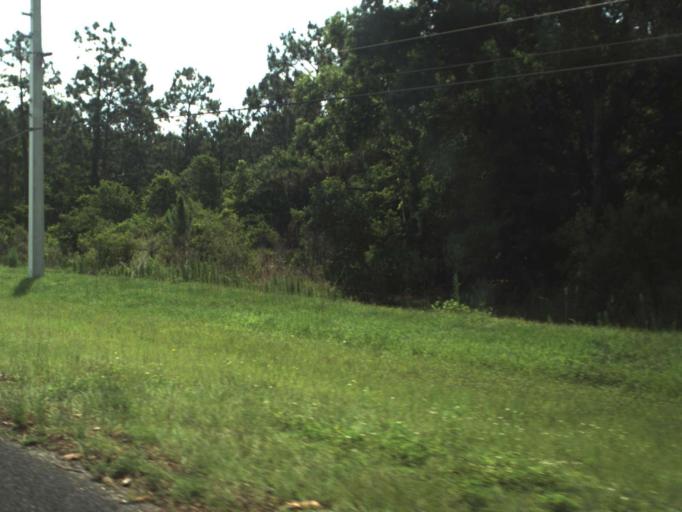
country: US
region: Florida
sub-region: Volusia County
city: Lake Helen
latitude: 29.0293
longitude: -81.1810
